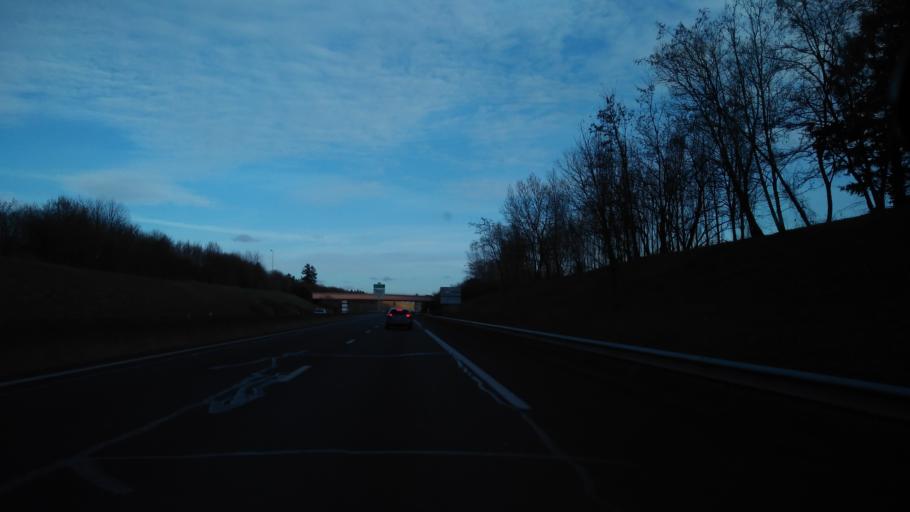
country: FR
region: Rhone-Alpes
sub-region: Departement du Rhone
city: Corbas
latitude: 45.6808
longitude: 4.8916
